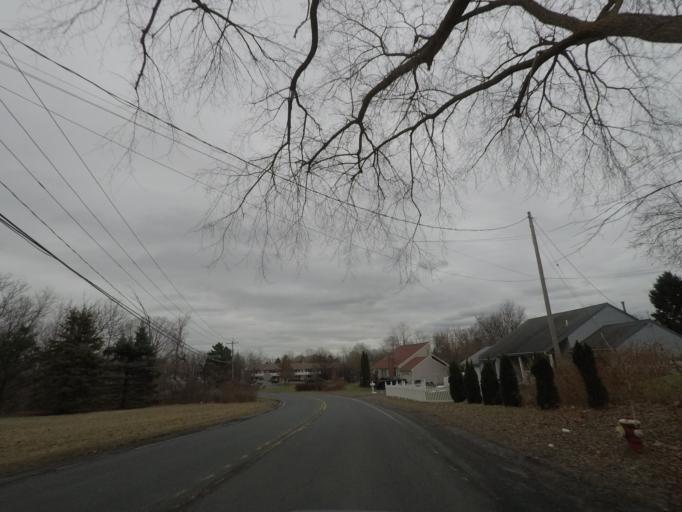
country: US
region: New York
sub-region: Albany County
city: Cohoes
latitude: 42.7638
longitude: -73.7368
